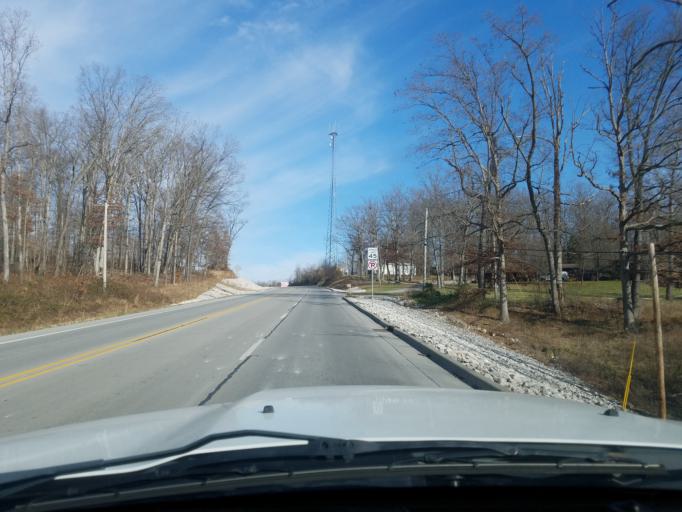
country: US
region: Indiana
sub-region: Orange County
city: Paoli
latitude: 38.5692
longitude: -86.4630
